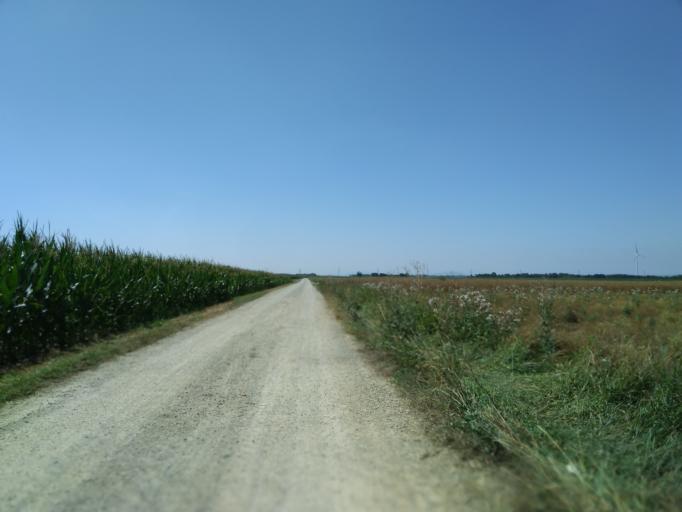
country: AT
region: Lower Austria
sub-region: Politischer Bezirk Mistelbach
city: Gross-Engersdorf
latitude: 48.3260
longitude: 16.5706
